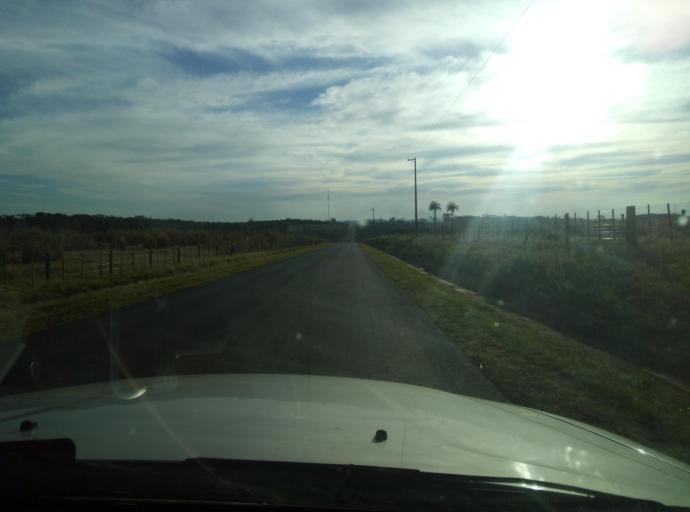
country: PY
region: Caaguazu
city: Carayao
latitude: -25.1549
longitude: -56.3143
